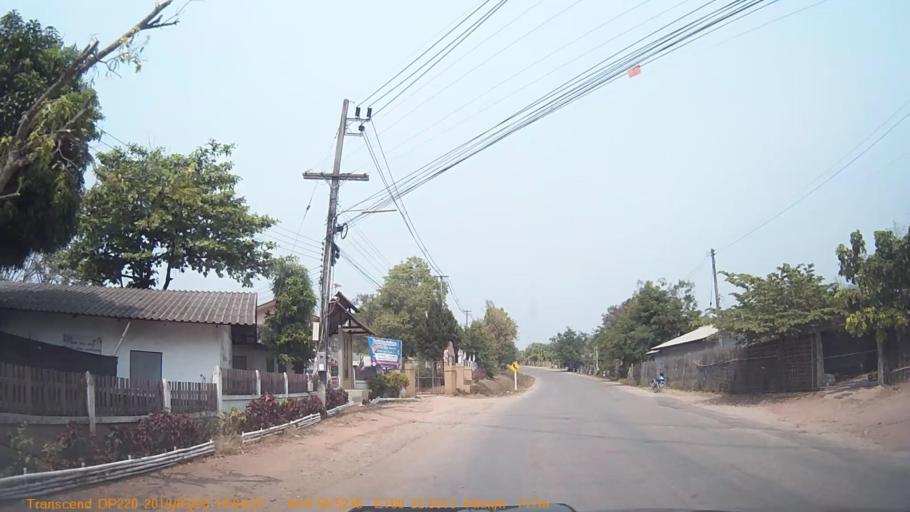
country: TH
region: Chiang Rai
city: Khun Tan
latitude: 19.8422
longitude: 100.3759
